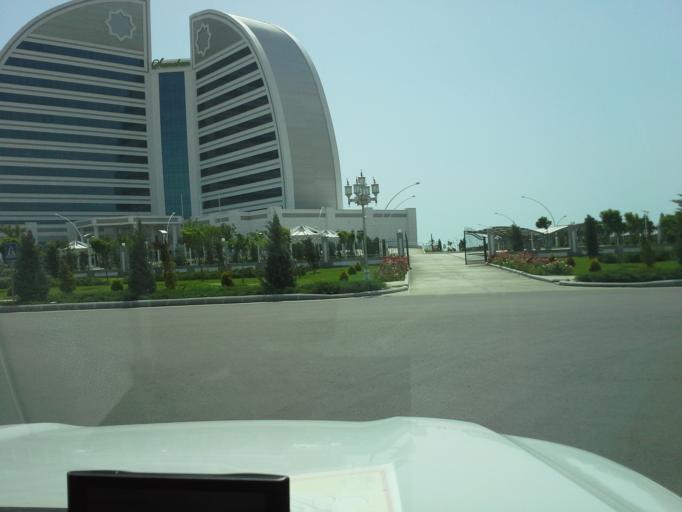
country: TM
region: Balkan
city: Turkmenbasy
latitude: 39.9758
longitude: 52.8291
